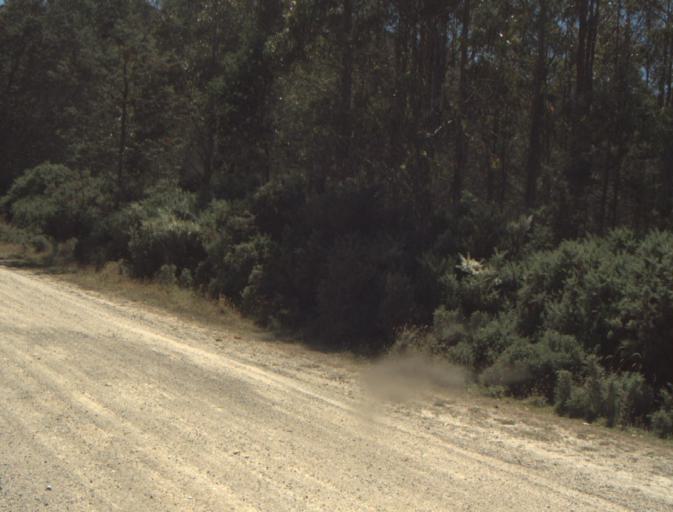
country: AU
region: Tasmania
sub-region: Dorset
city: Scottsdale
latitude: -41.3306
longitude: 147.4983
